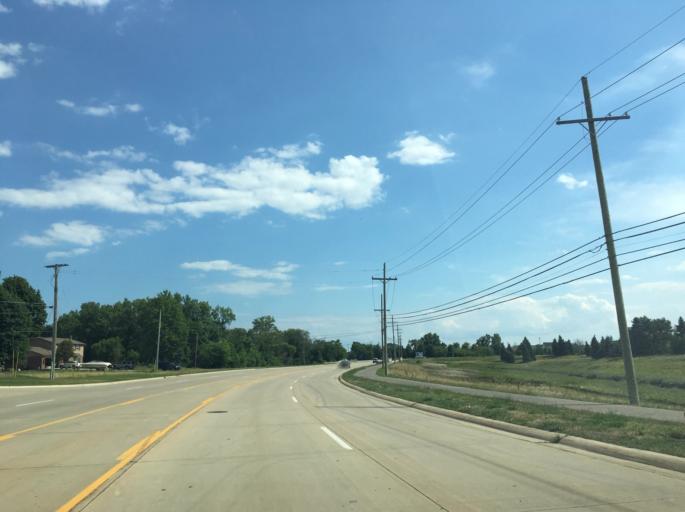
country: US
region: Michigan
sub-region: Macomb County
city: Clinton
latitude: 42.6227
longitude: -82.9350
